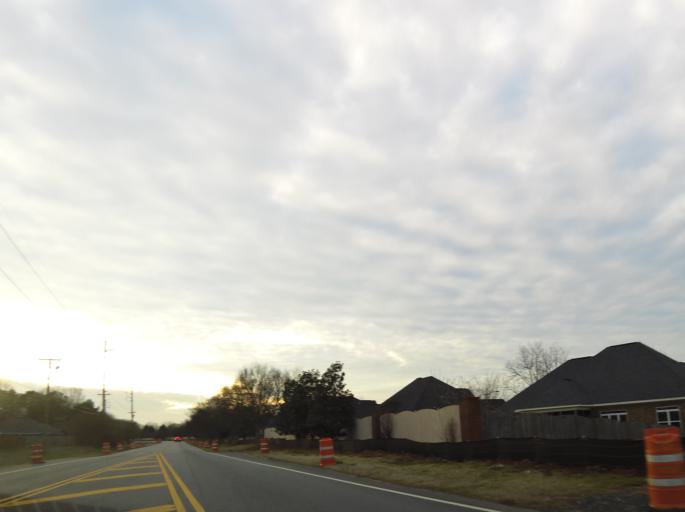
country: US
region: Georgia
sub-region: Houston County
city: Centerville
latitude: 32.6240
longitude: -83.6966
